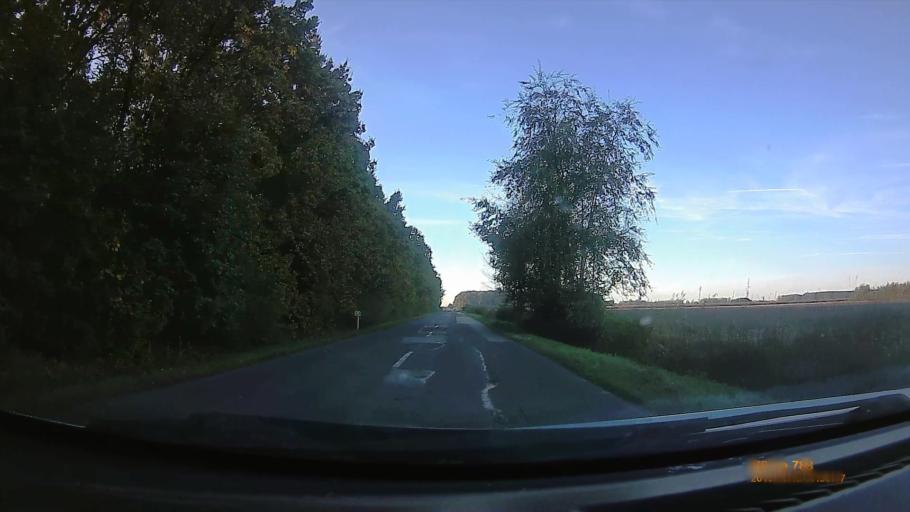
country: HU
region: Hajdu-Bihar
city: Biharkeresztes
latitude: 47.1540
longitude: 21.7388
